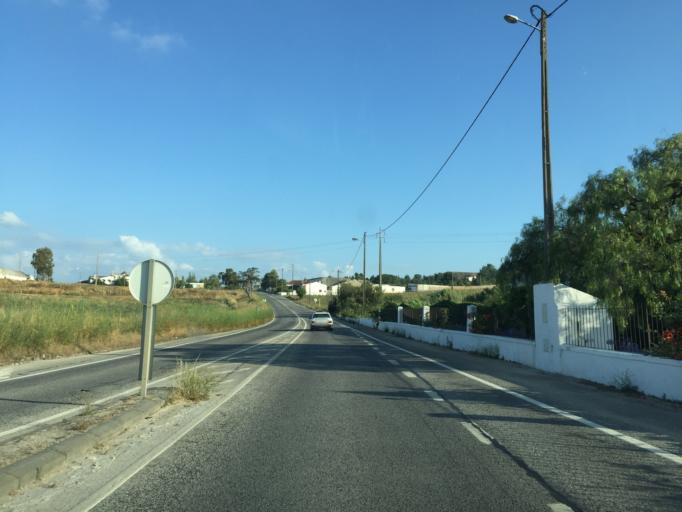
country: PT
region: Lisbon
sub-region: Azambuja
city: Alcoentre
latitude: 39.1360
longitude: -8.9979
